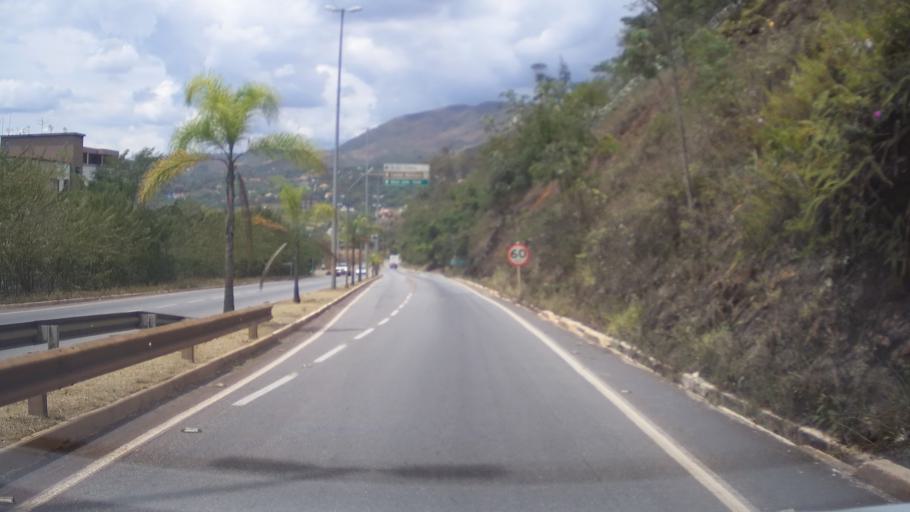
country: BR
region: Minas Gerais
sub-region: Nova Lima
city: Nova Lima
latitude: -19.9943
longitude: -43.8581
